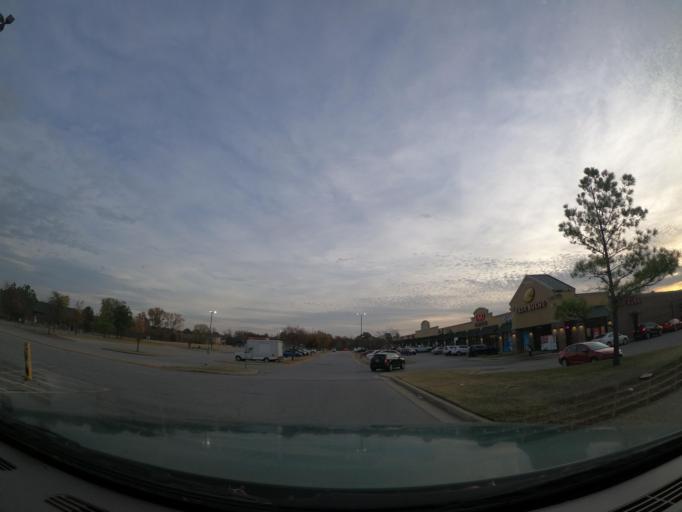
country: US
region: Oklahoma
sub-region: Tulsa County
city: Broken Arrow
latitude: 35.9905
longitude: -95.7999
